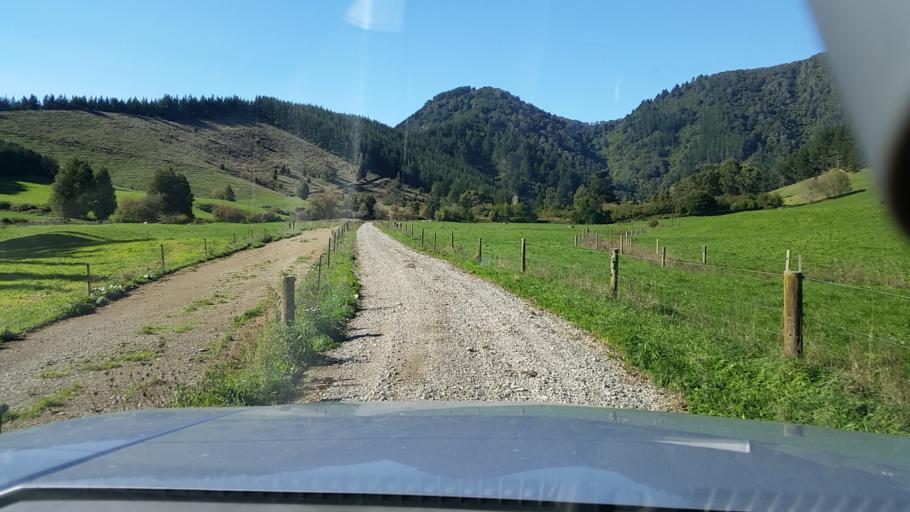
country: NZ
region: Nelson
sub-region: Nelson City
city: Nelson
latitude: -41.2220
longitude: 173.6068
